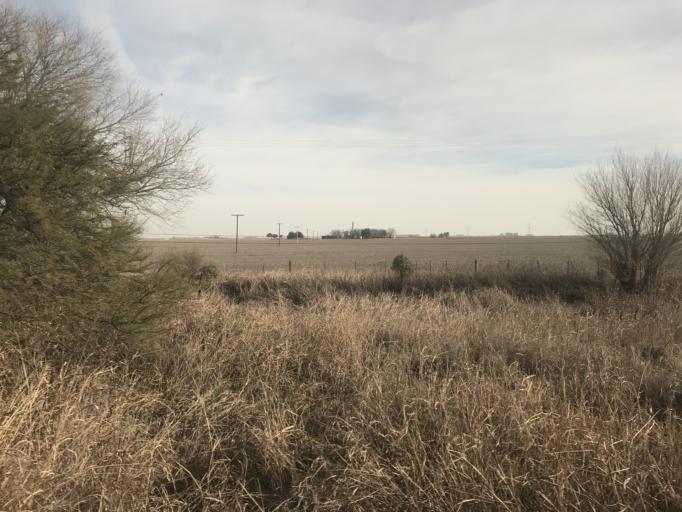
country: AR
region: Cordoba
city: Pilar
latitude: -31.7159
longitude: -63.8563
